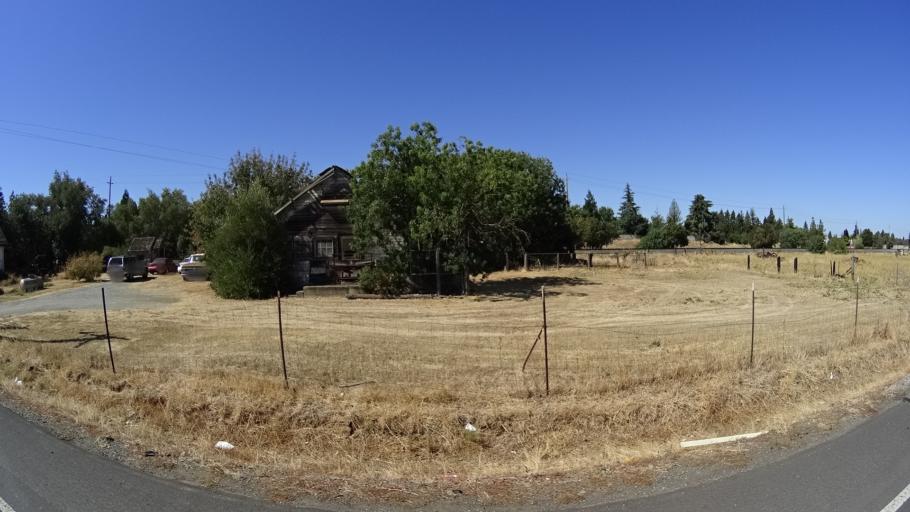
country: US
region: California
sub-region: Sacramento County
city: Elk Grove
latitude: 38.4306
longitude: -121.3716
